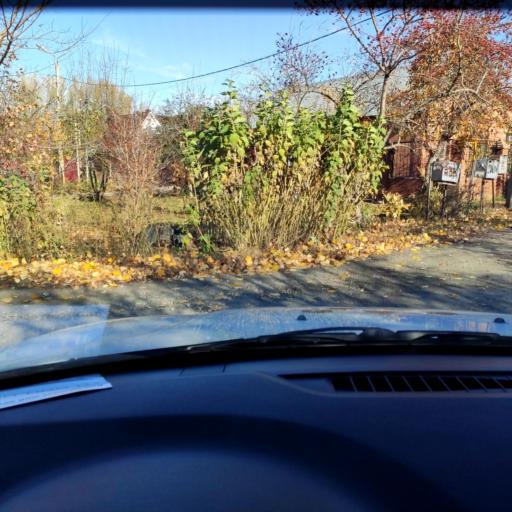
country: RU
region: Samara
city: Tol'yatti
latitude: 53.5395
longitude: 49.4161
